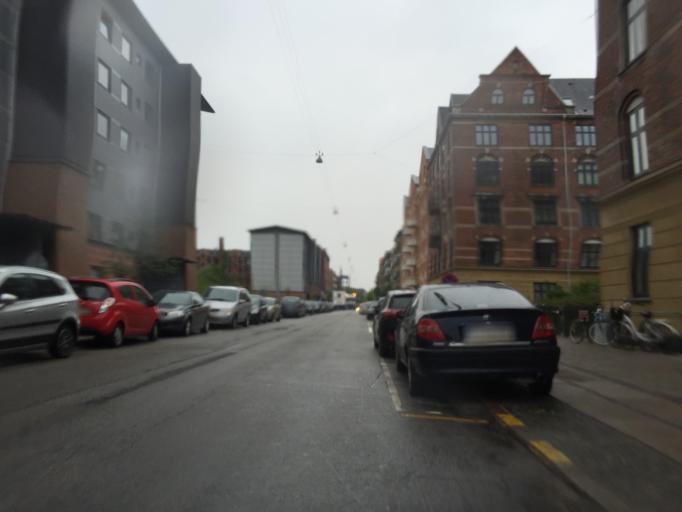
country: DK
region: Capital Region
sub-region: Frederiksberg Kommune
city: Frederiksberg
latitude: 55.6904
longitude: 12.5339
